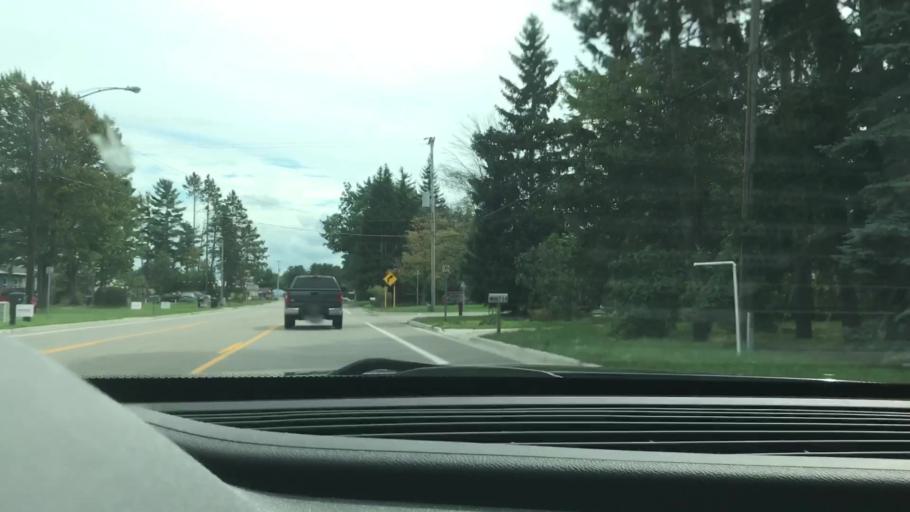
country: US
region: Michigan
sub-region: Missaukee County
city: Lake City
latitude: 44.3224
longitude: -85.2119
